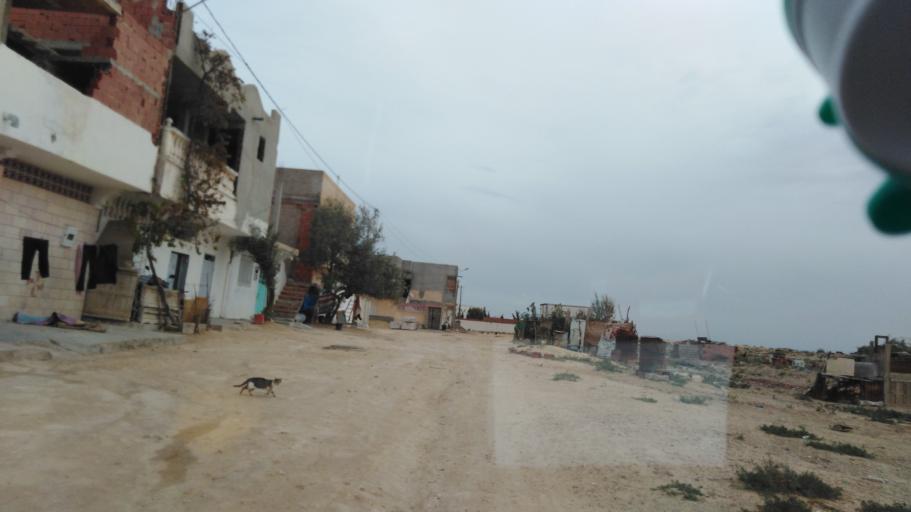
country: TN
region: Qabis
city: Gabes
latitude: 33.9487
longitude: 10.0023
